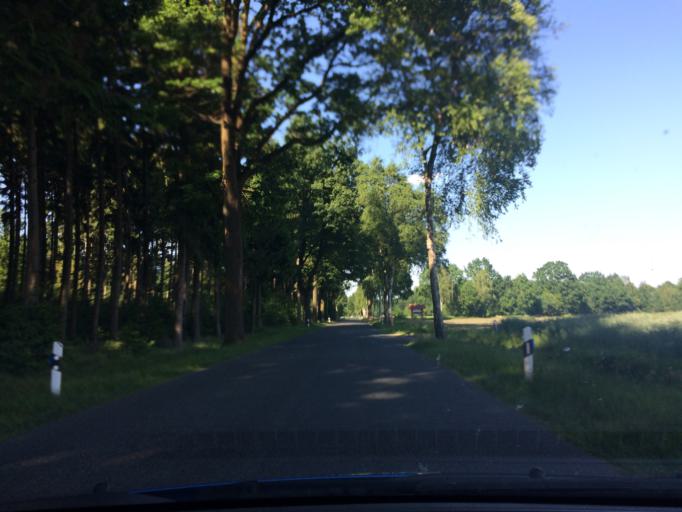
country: DE
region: Lower Saxony
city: Neuenkirchen
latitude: 52.9604
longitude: 9.7043
